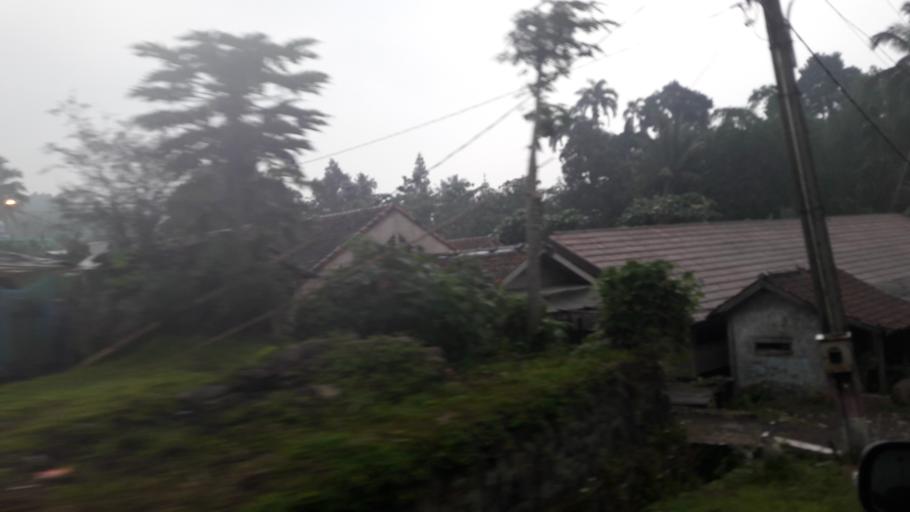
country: ID
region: West Java
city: Cipeundeuy
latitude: -6.6469
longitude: 106.5214
